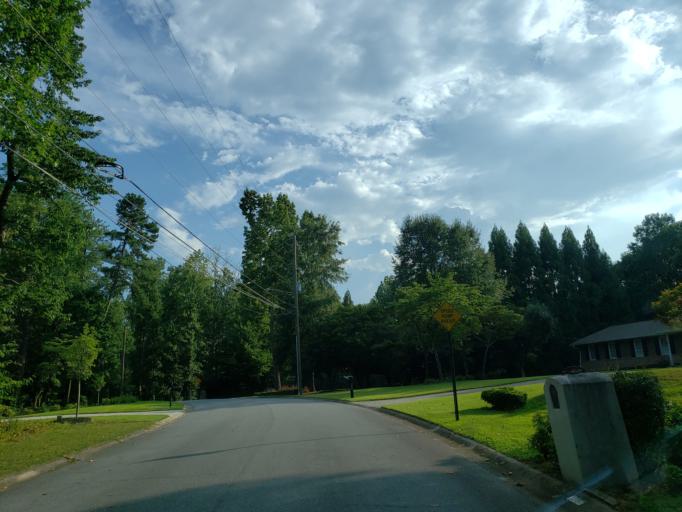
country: US
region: Georgia
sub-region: Cobb County
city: Kennesaw
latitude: 34.0467
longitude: -84.5912
